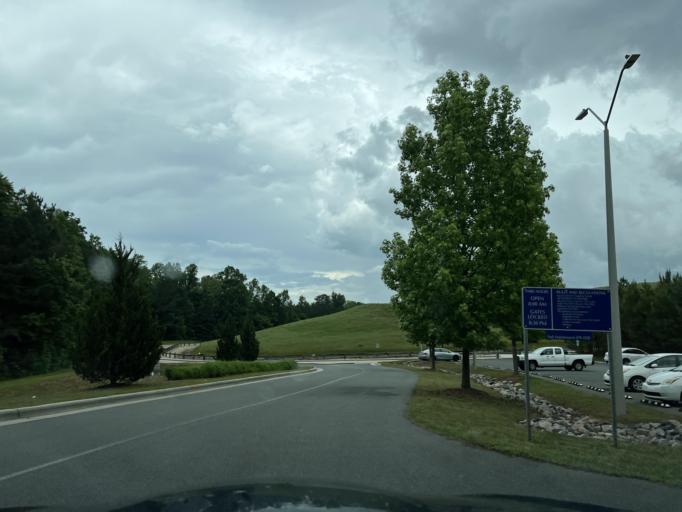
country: US
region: North Carolina
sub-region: Wake County
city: Wake Forest
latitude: 35.9061
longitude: -78.5843
